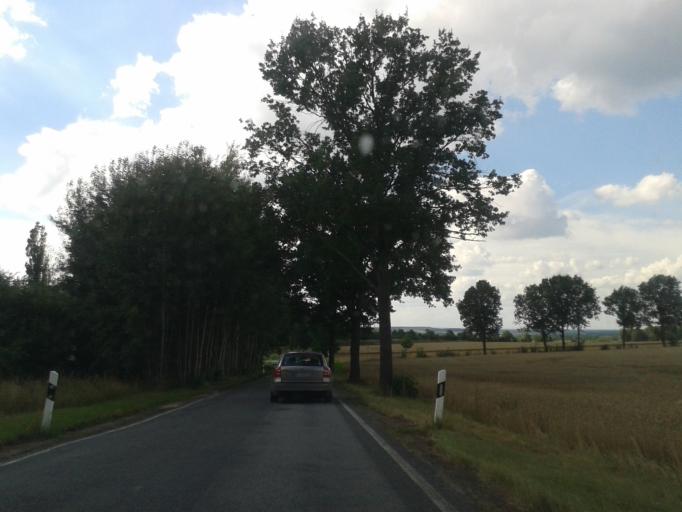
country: DE
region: Saxony
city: Radibor
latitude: 51.2039
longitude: 14.3773
